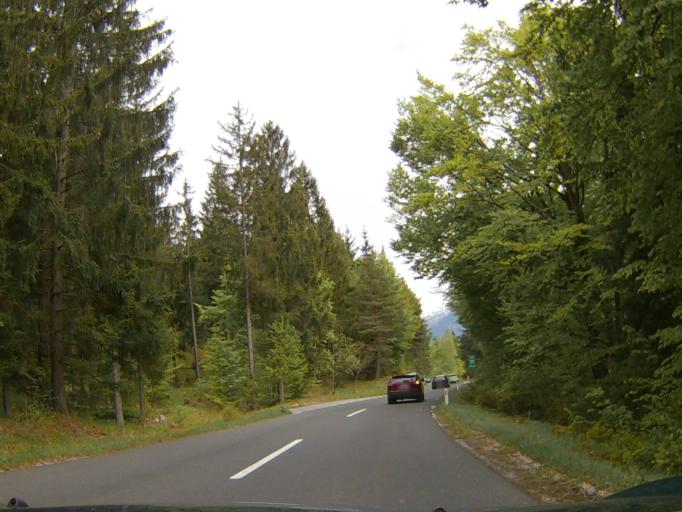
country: AT
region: Carinthia
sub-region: Villach Stadt
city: Villach
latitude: 46.5782
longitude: 13.7884
